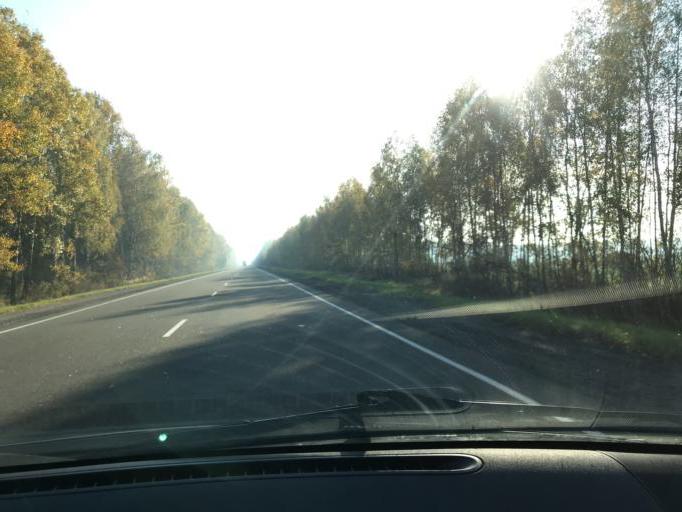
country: BY
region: Brest
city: Horad Luninyets
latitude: 52.3027
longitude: 26.7110
